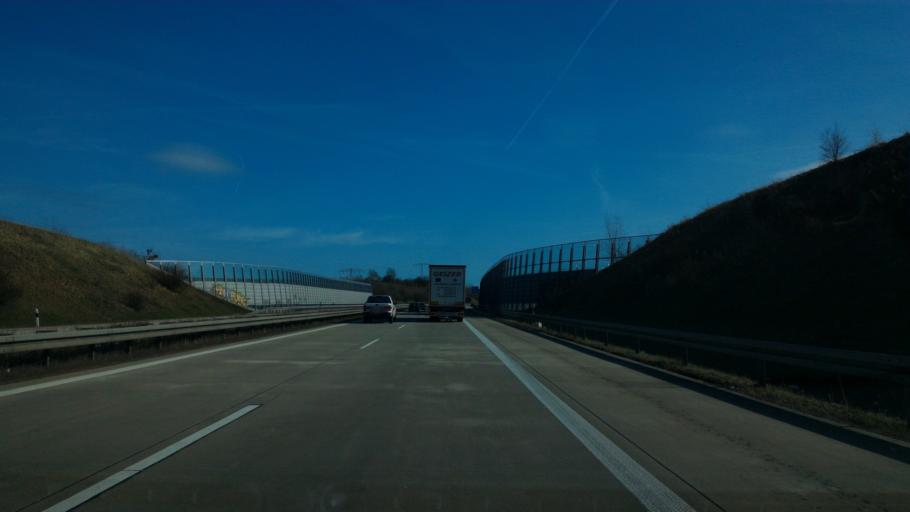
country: DE
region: Saxony
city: Dohna
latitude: 50.9598
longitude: 13.8621
